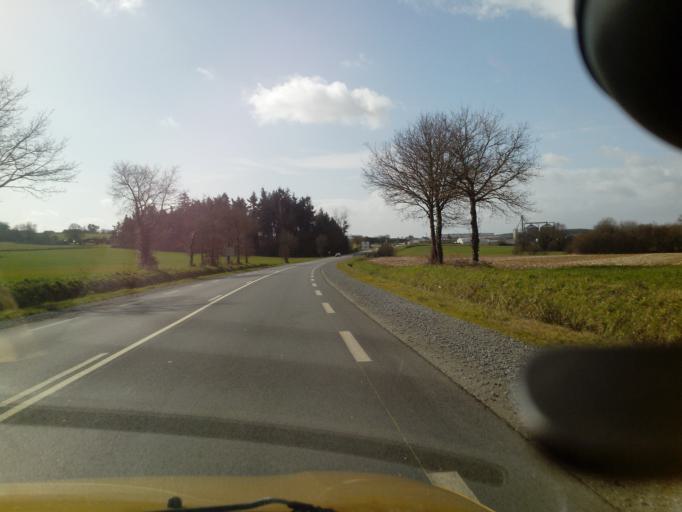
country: FR
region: Brittany
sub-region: Departement du Morbihan
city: Mauron
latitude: 48.0752
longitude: -2.2749
